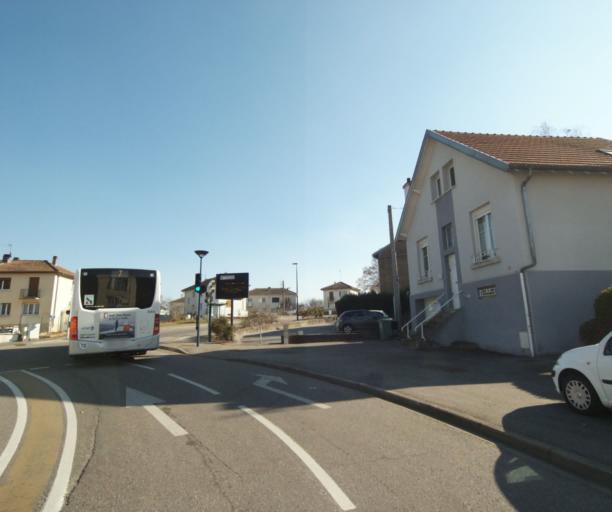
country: FR
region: Lorraine
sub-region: Departement de Meurthe-et-Moselle
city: Vandoeuvre-les-Nancy
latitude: 48.6446
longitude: 6.1759
